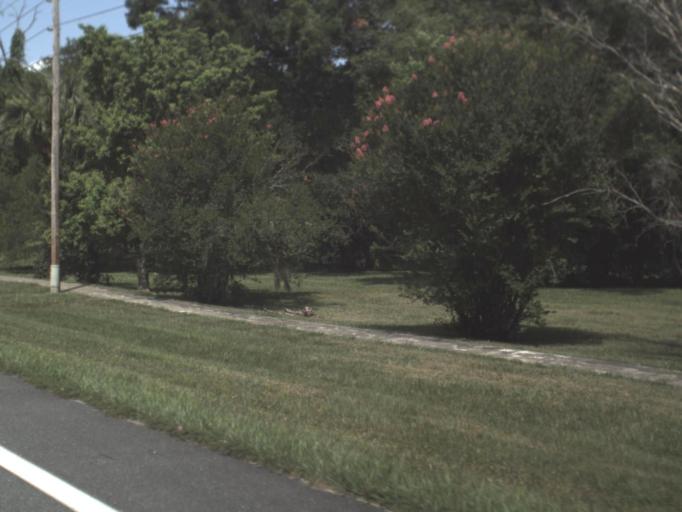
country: US
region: Florida
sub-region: Levy County
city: Williston
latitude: 29.3969
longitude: -82.4447
